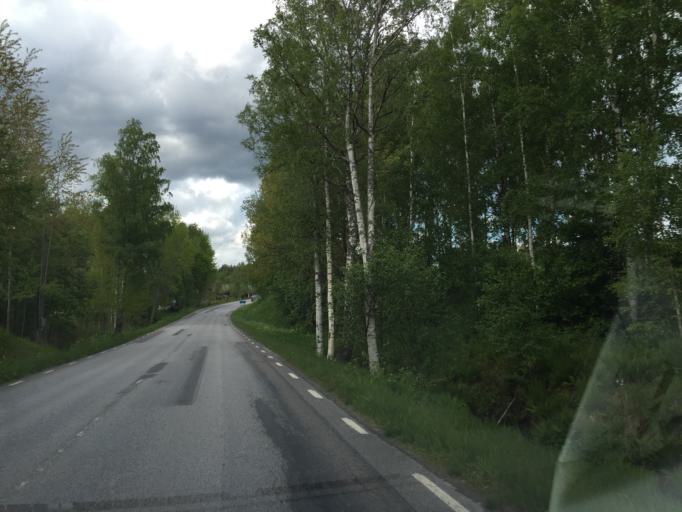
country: SE
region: OEstergoetland
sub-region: Finspangs Kommun
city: Finspang
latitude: 58.6766
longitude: 15.7527
